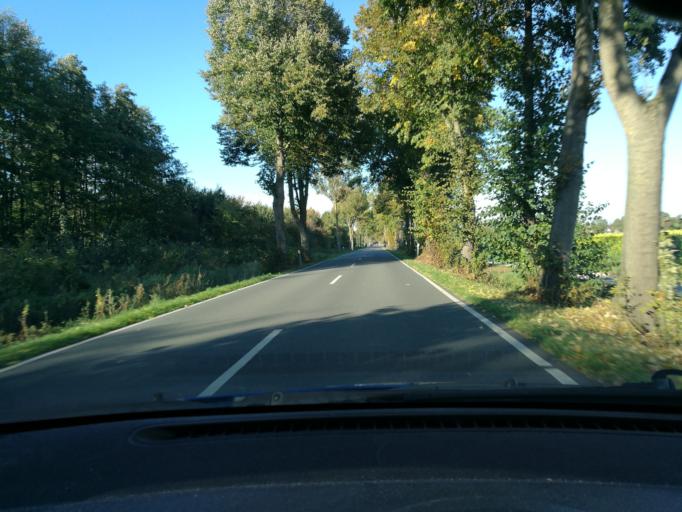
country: DE
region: Lower Saxony
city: Ludersburg
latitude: 53.3112
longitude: 10.5723
